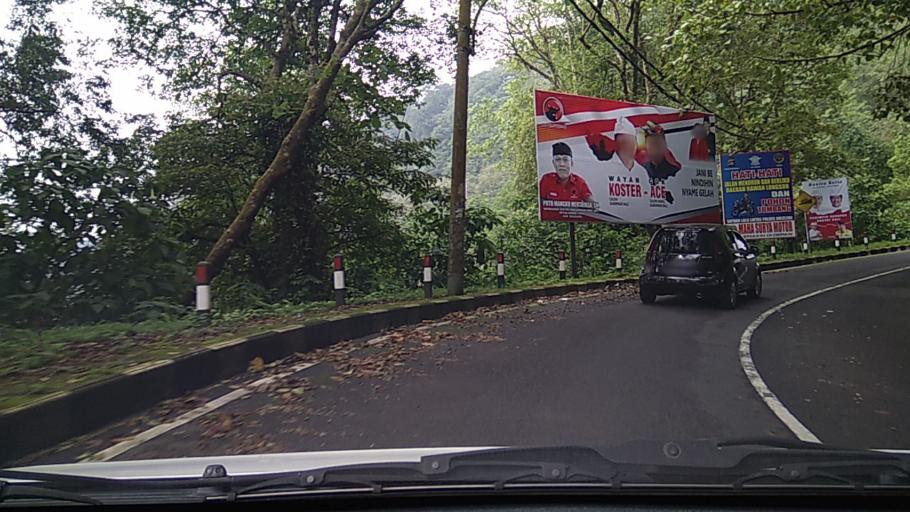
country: ID
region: Bali
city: Munduk
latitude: -8.2402
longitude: 115.1445
